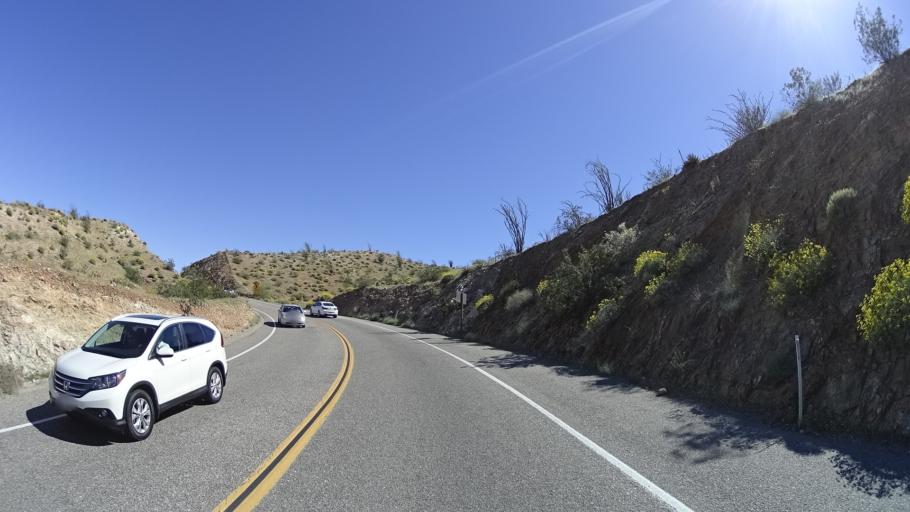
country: US
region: California
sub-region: San Diego County
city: Borrego Springs
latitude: 33.2417
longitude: -116.4053
